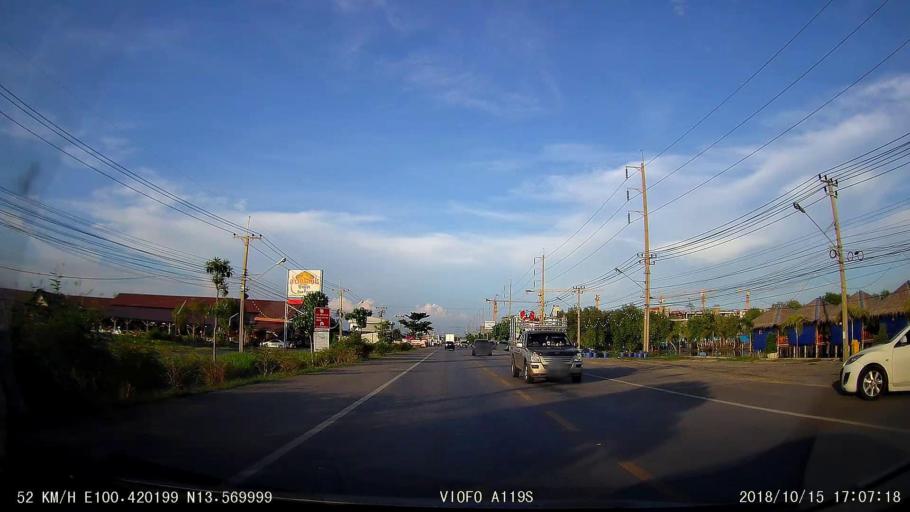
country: TH
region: Bangkok
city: Bang Khun Thian
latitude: 13.5701
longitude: 100.4203
